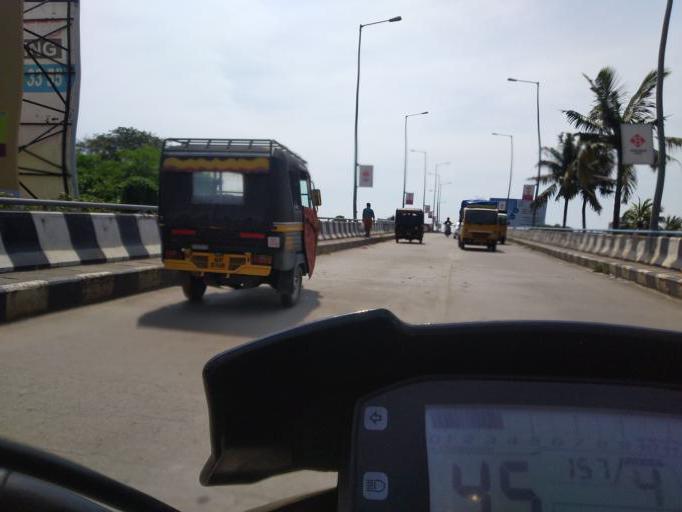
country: IN
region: Kerala
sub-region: Ernakulam
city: Cochin
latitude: 9.9765
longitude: 76.2906
